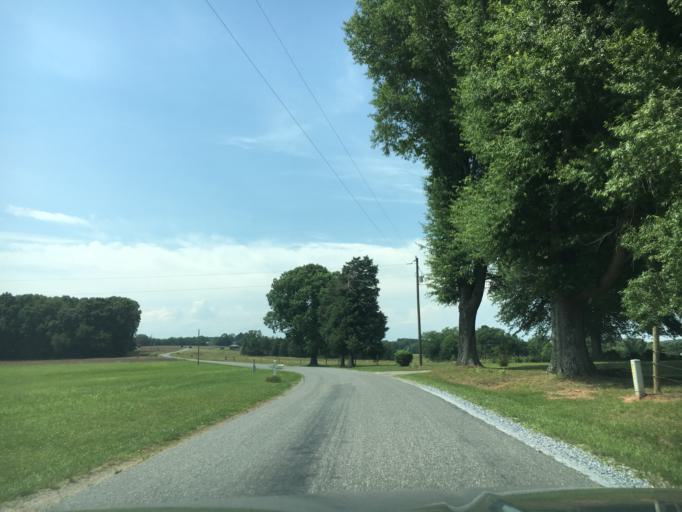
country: US
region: Virginia
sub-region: Pittsylvania County
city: Gretna
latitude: 36.9176
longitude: -79.4224
